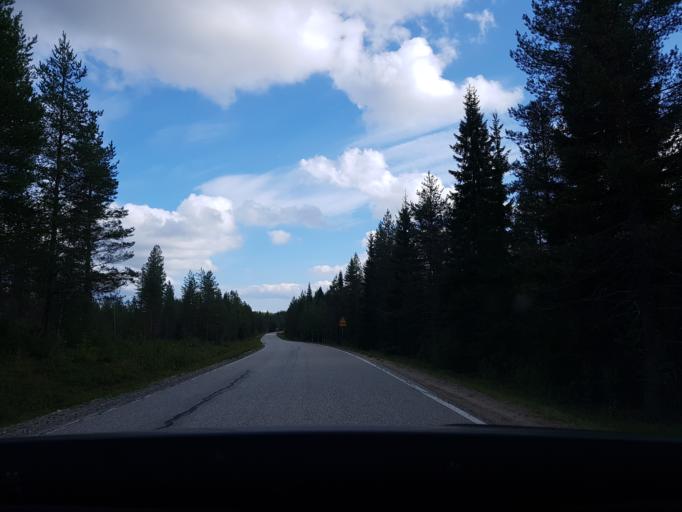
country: FI
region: Kainuu
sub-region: Kehys-Kainuu
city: Kuhmo
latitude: 64.6294
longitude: 29.6917
